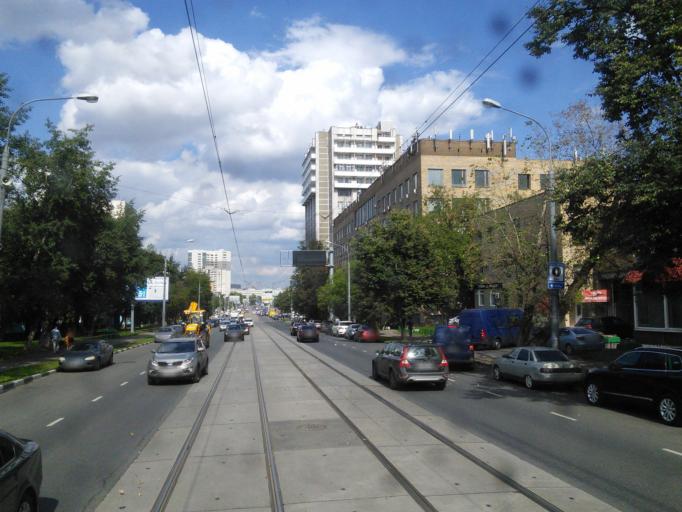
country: RU
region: Moscow
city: Novyye Cheremushki
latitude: 55.7042
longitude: 37.5835
